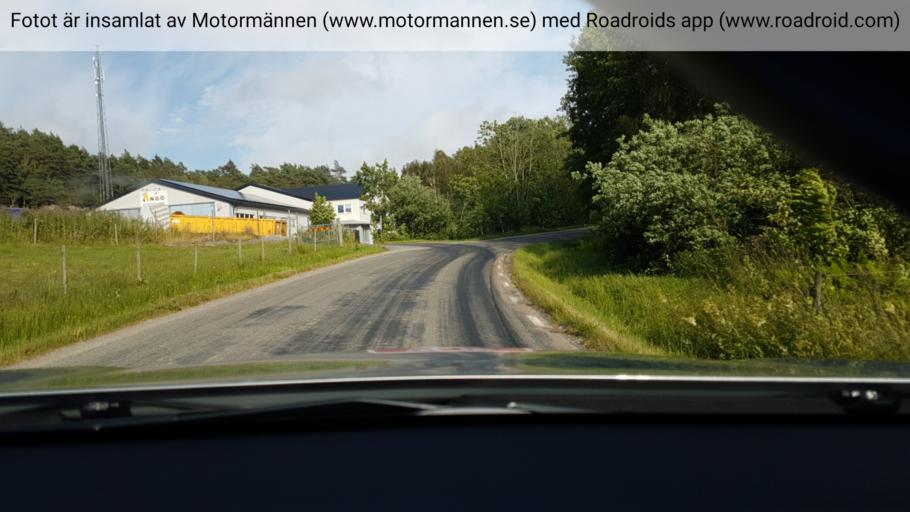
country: SE
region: Vaestra Goetaland
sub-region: Tjorns Kommun
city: Myggenas
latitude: 58.1295
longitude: 11.6633
